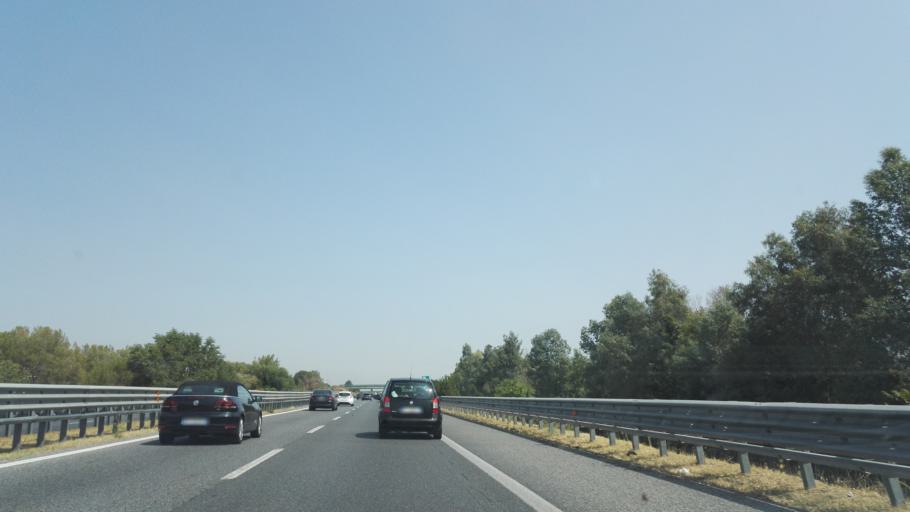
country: IT
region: Calabria
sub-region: Provincia di Cosenza
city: Stazione Montalto-Coretto
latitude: 39.3993
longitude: 16.2434
